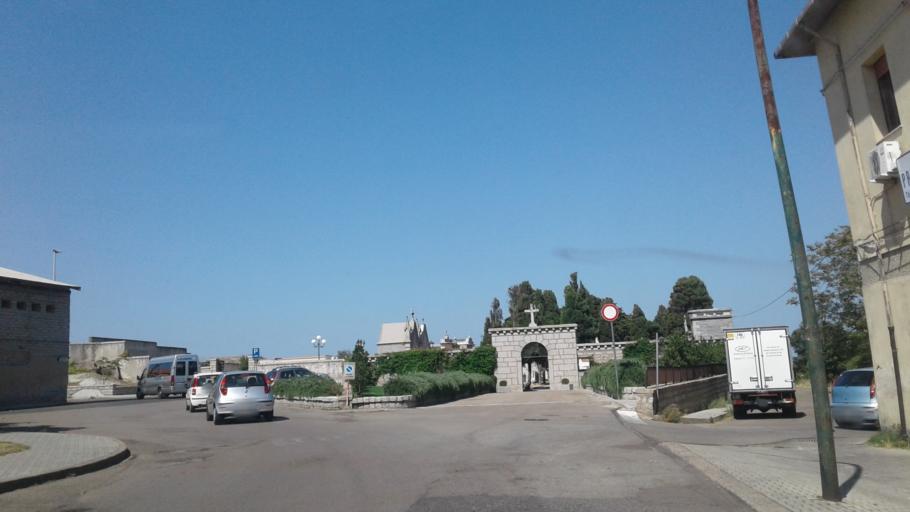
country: IT
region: Sardinia
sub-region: Provincia di Olbia-Tempio
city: Tempio Pausania
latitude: 40.9059
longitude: 9.1070
